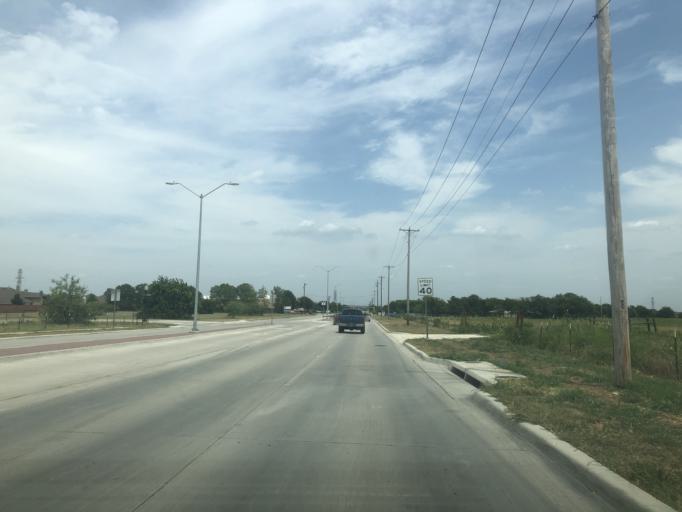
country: US
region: Texas
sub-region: Tarrant County
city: Saginaw
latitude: 32.8837
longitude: -97.3610
